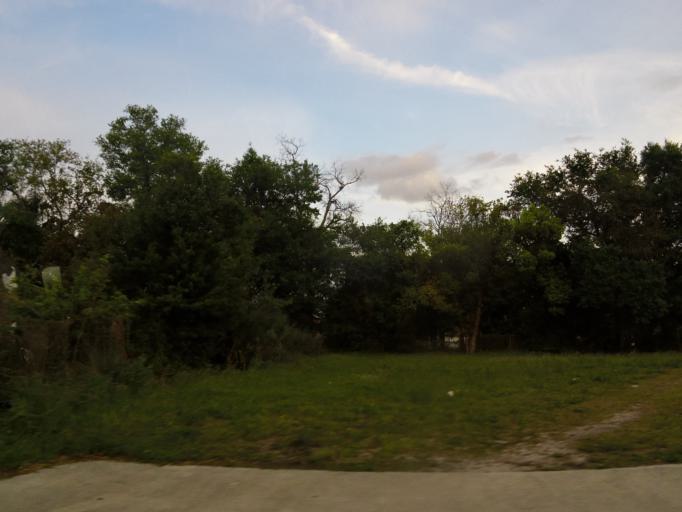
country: US
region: Florida
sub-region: Duval County
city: Jacksonville
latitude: 30.3583
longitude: -81.6370
